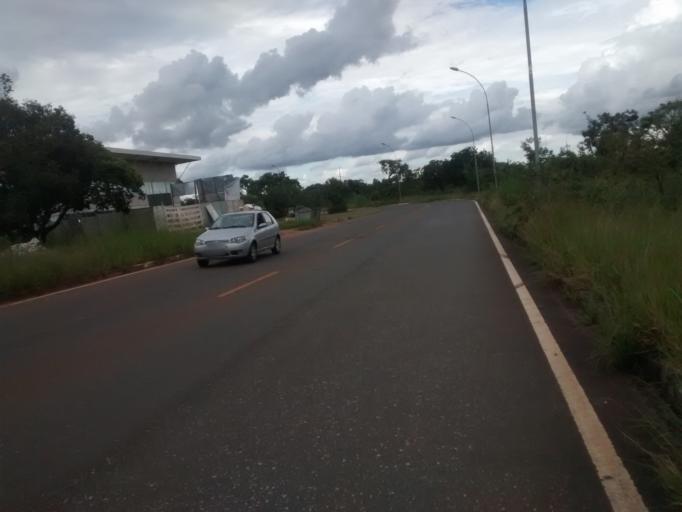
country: BR
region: Federal District
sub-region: Brasilia
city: Brasilia
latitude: -15.7751
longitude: -47.8676
